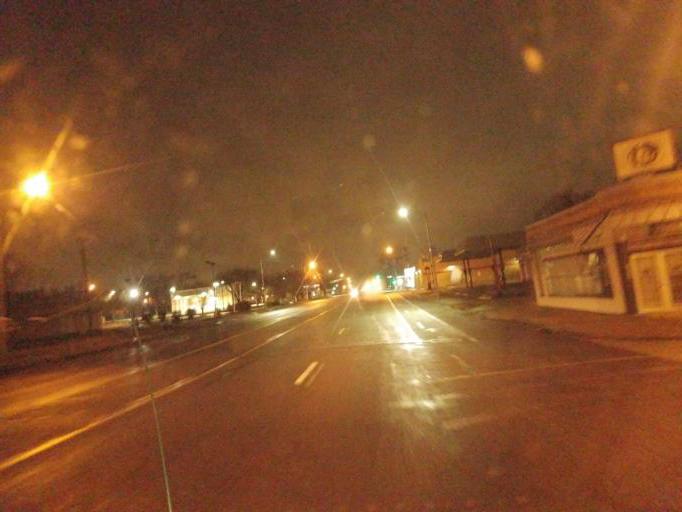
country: US
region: Missouri
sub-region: City of Saint Louis
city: St. Louis
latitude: 38.6490
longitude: -90.1991
